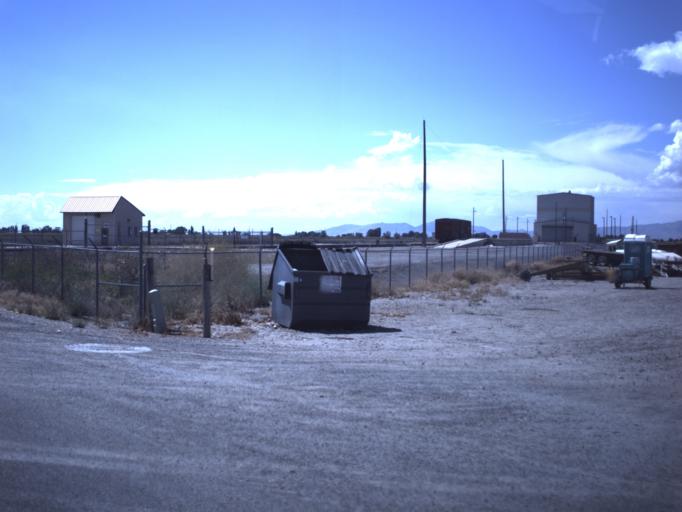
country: US
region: Utah
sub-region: Box Elder County
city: Honeyville
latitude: 41.5640
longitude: -112.1296
